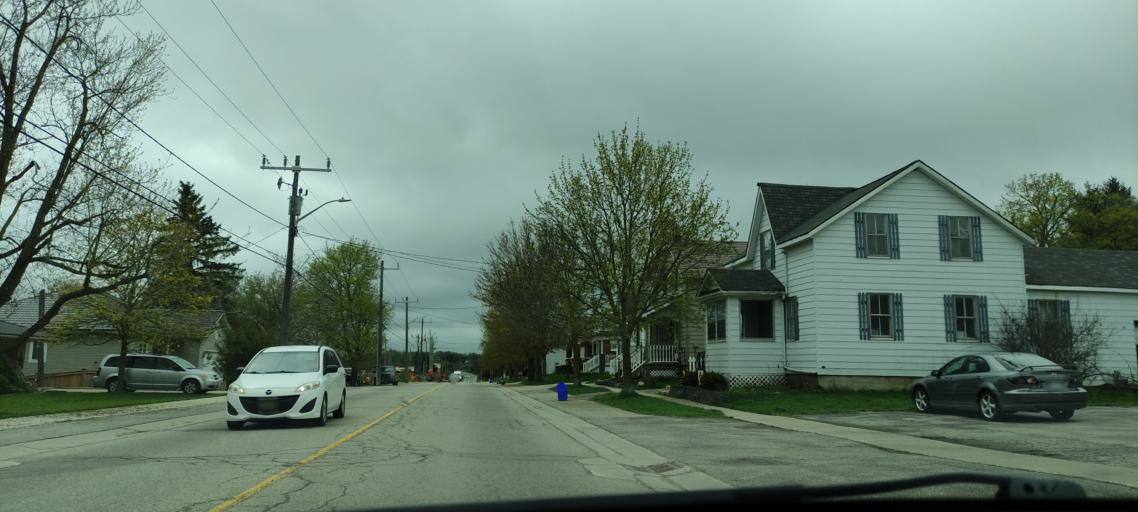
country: CA
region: Ontario
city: Stratford
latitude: 43.4726
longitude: -80.7649
